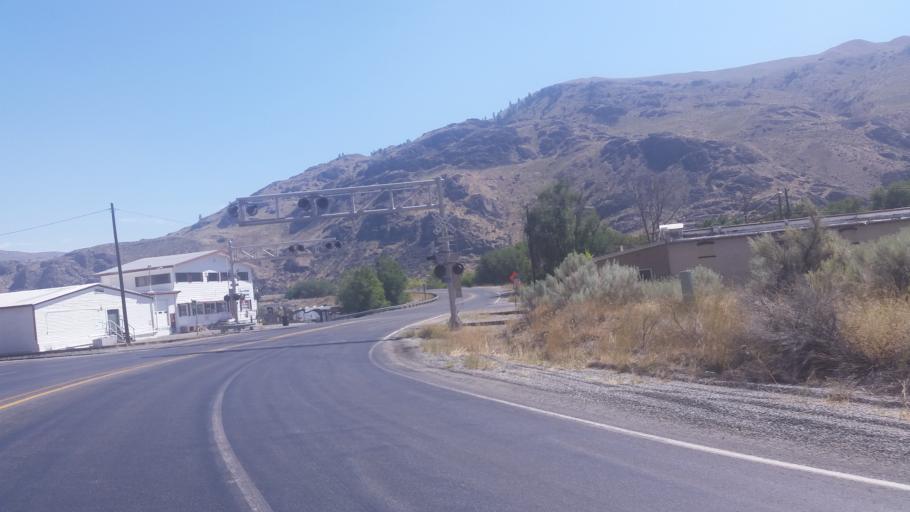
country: US
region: Washington
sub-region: Chelan County
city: Chelan
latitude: 47.8171
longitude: -119.9783
